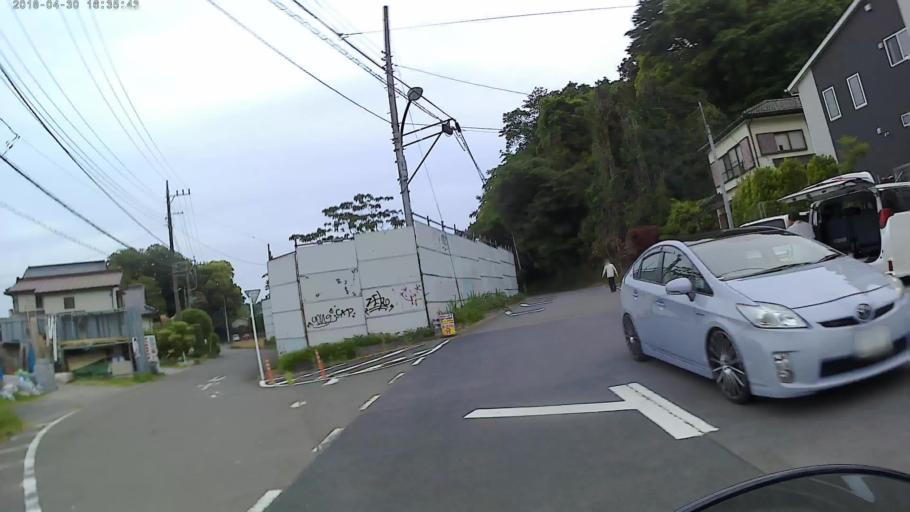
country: JP
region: Kanagawa
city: Atsugi
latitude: 35.4406
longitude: 139.4107
